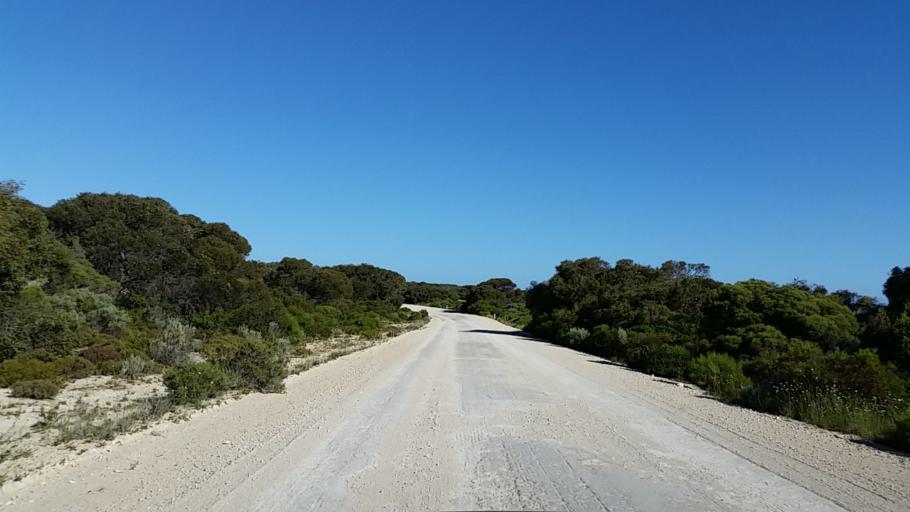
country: AU
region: South Australia
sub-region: Yorke Peninsula
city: Honiton
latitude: -35.2287
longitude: 137.1078
